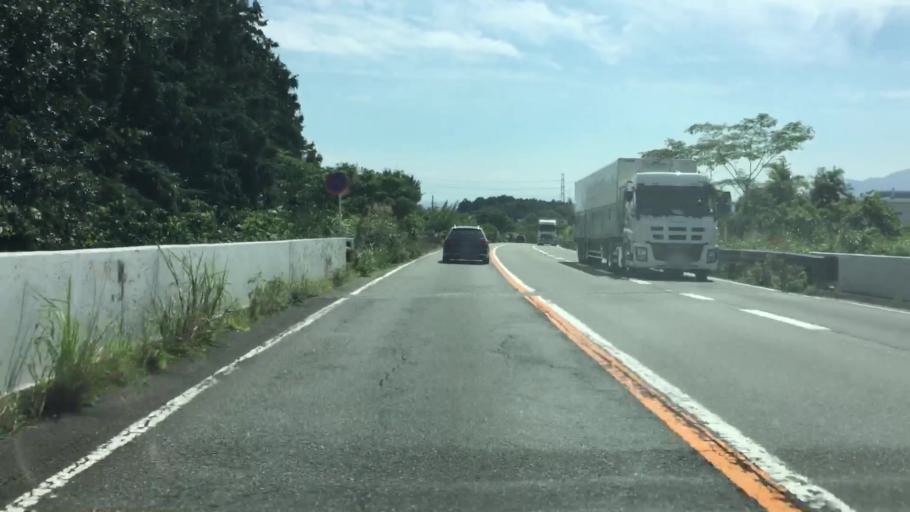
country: JP
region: Shizuoka
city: Fujinomiya
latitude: 35.2701
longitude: 138.6144
